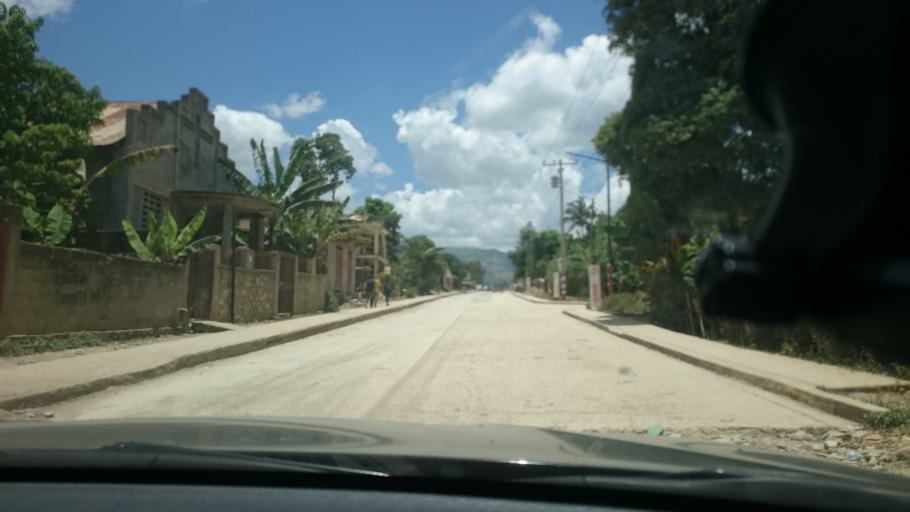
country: HT
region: Nord
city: Dondon
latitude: 19.5499
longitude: -72.2372
